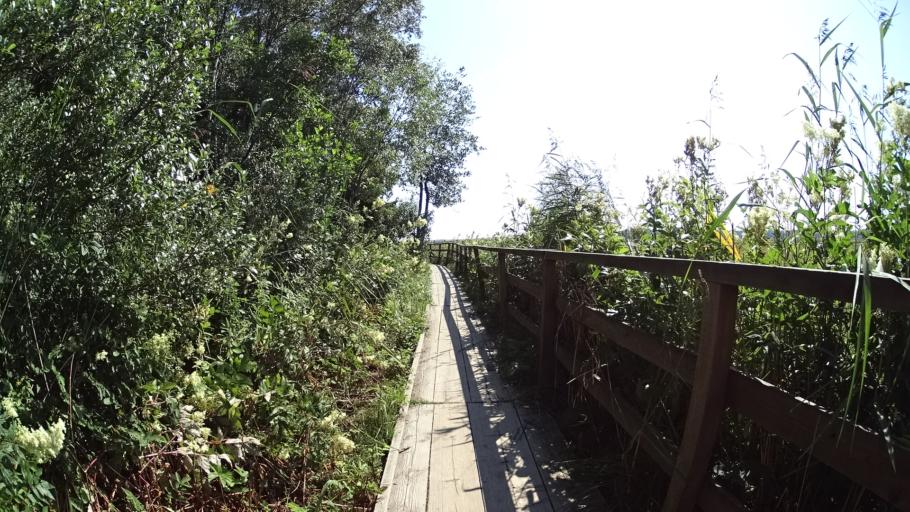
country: FI
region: Uusimaa
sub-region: Helsinki
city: Teekkarikylae
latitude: 60.2000
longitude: 24.8225
